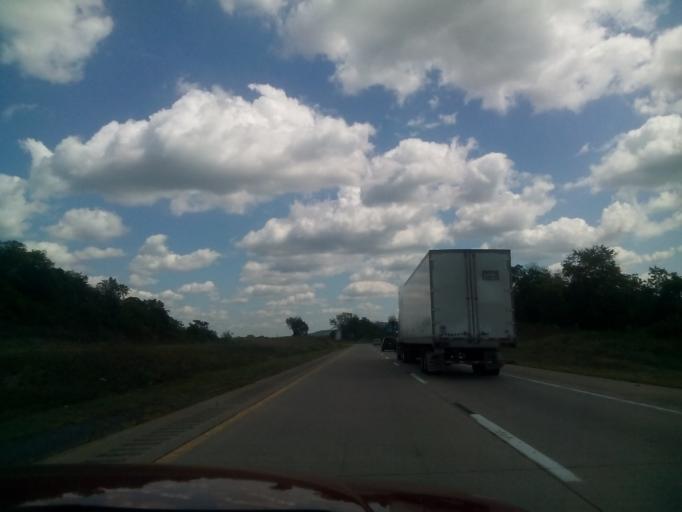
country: US
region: Pennsylvania
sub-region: Northumberland County
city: Riverside
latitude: 40.9898
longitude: -76.6666
